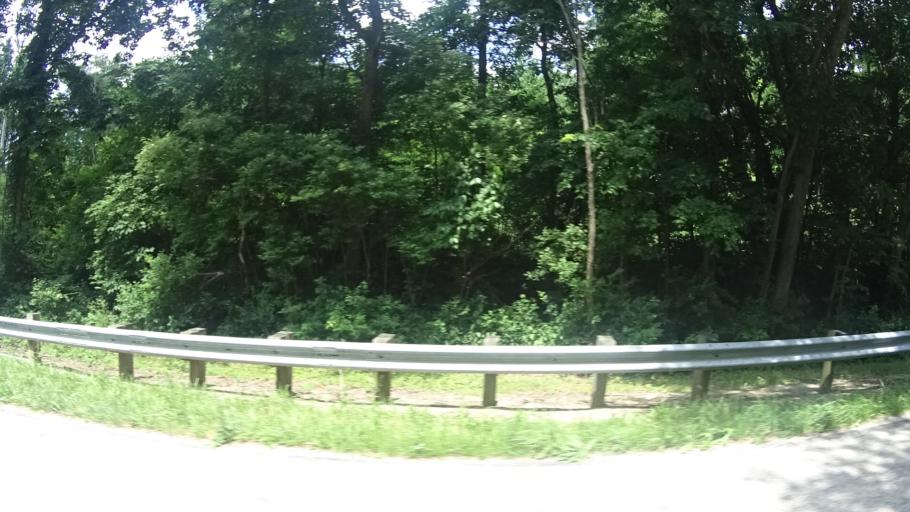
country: US
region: Ohio
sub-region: Erie County
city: Huron
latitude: 41.3193
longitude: -82.5279
